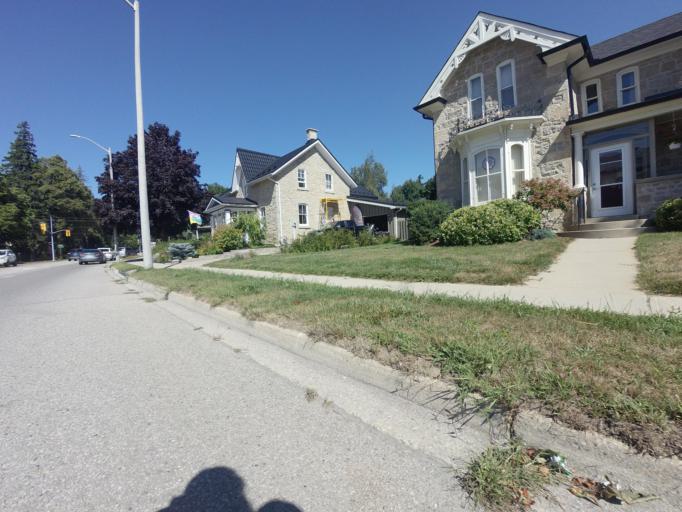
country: CA
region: Ontario
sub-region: Wellington County
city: Guelph
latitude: 43.7073
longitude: -80.3814
